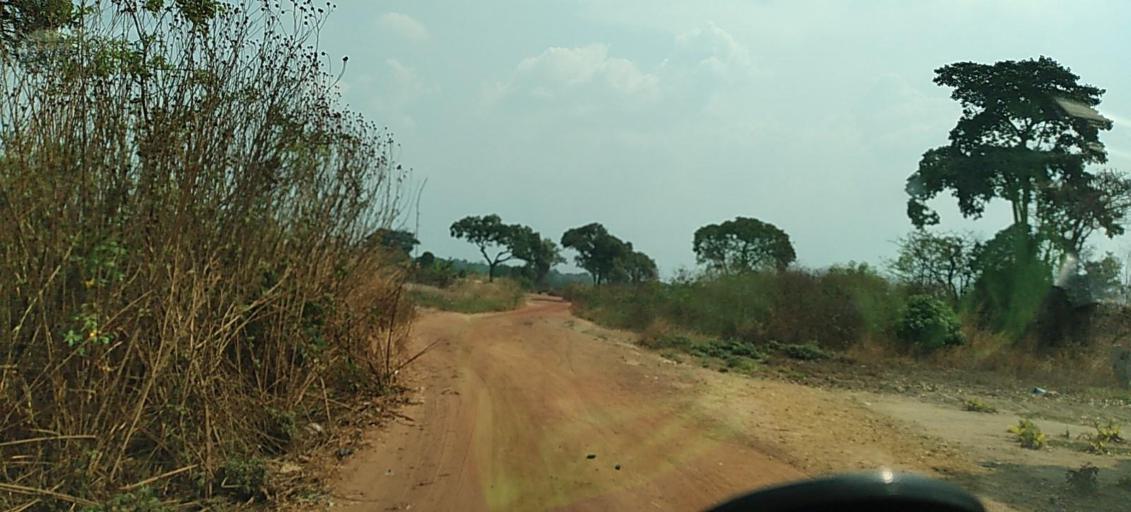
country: ZM
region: North-Western
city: Kansanshi
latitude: -12.0936
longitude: 26.3646
